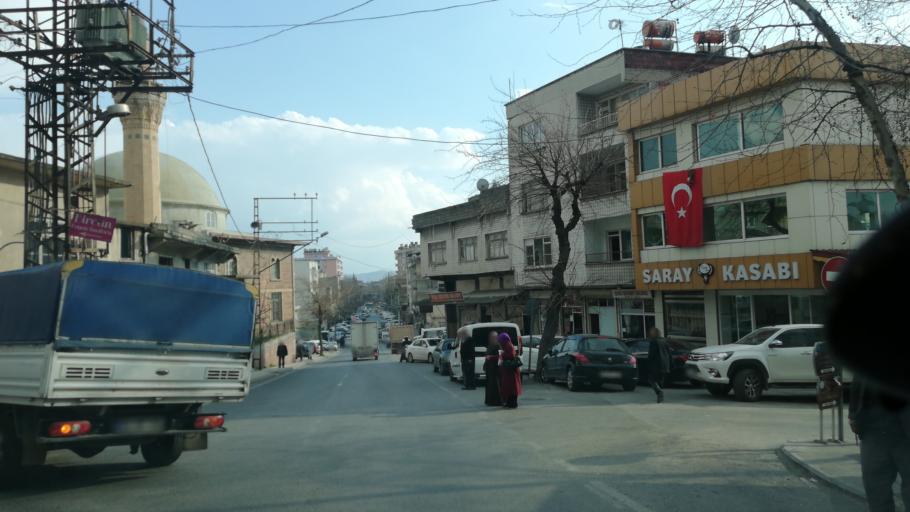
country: TR
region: Kahramanmaras
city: Kahramanmaras
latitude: 37.5820
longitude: 36.9313
